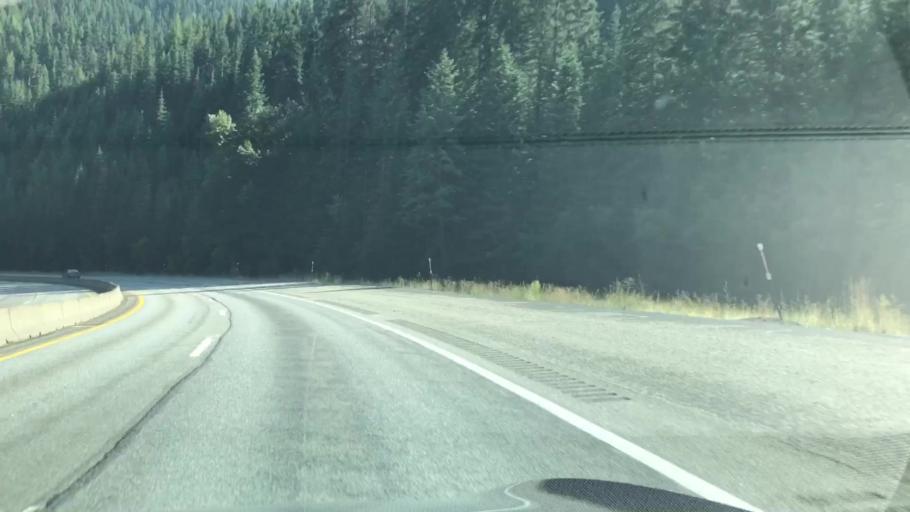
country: US
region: Idaho
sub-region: Shoshone County
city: Pinehurst
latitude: 47.5927
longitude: -116.4930
